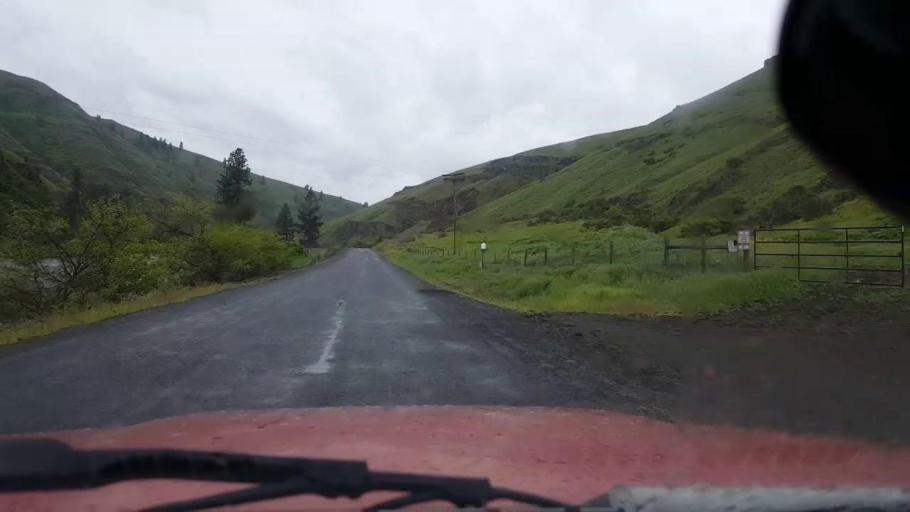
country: US
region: Washington
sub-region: Asotin County
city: Asotin
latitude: 46.0257
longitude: -117.3352
